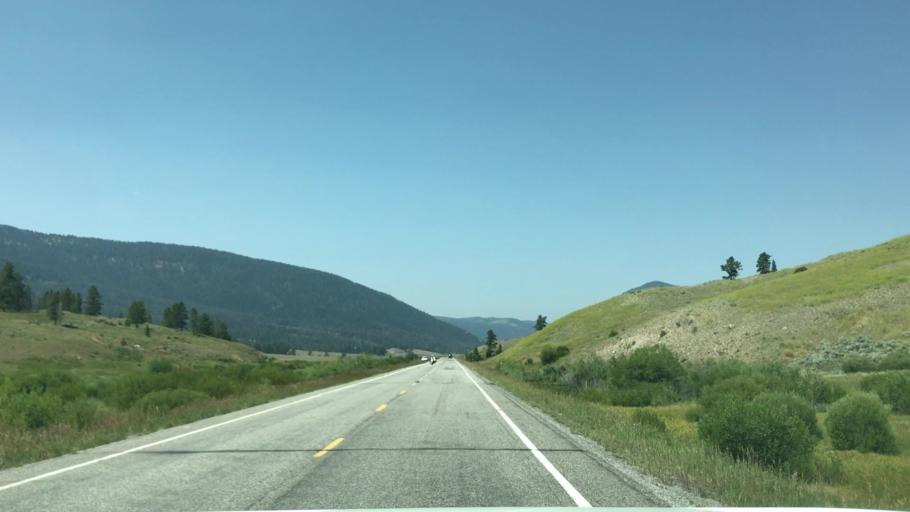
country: US
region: Montana
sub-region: Gallatin County
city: Big Sky
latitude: 45.0397
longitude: -111.1221
